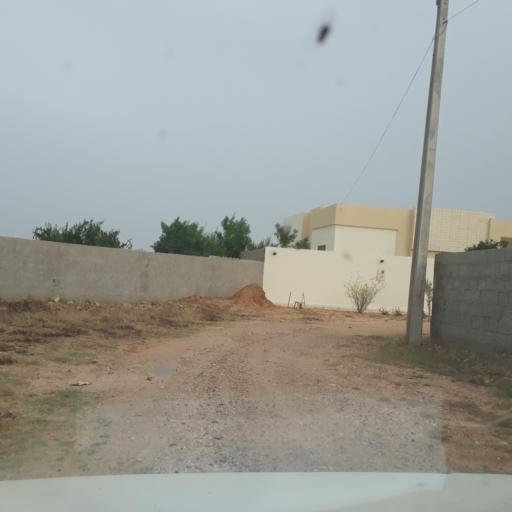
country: TN
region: Safaqis
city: Al Qarmadah
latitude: 34.8232
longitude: 10.7754
